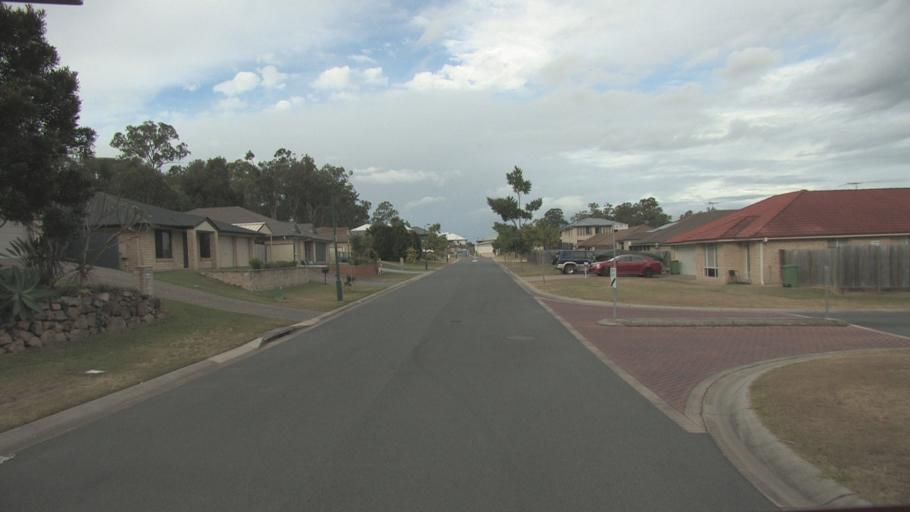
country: AU
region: Queensland
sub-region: Logan
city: Park Ridge South
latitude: -27.6782
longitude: 153.0268
